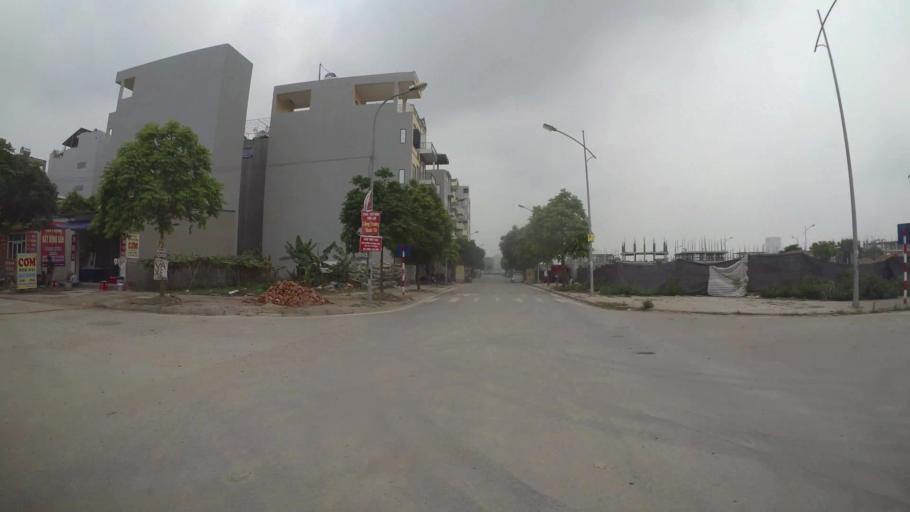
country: VN
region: Ha Noi
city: Ha Dong
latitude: 20.9854
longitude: 105.7522
